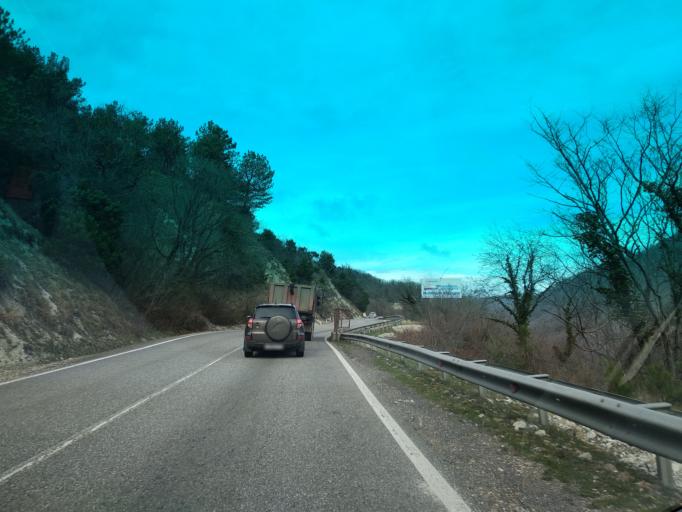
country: RU
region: Krasnodarskiy
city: Shepsi
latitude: 44.0640
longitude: 39.1361
